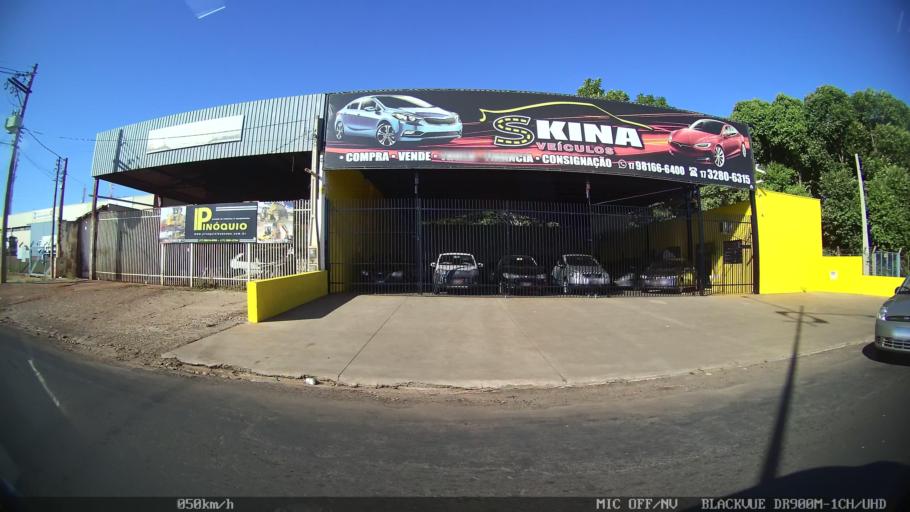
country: BR
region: Sao Paulo
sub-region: Olimpia
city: Olimpia
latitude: -20.7309
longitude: -48.9049
